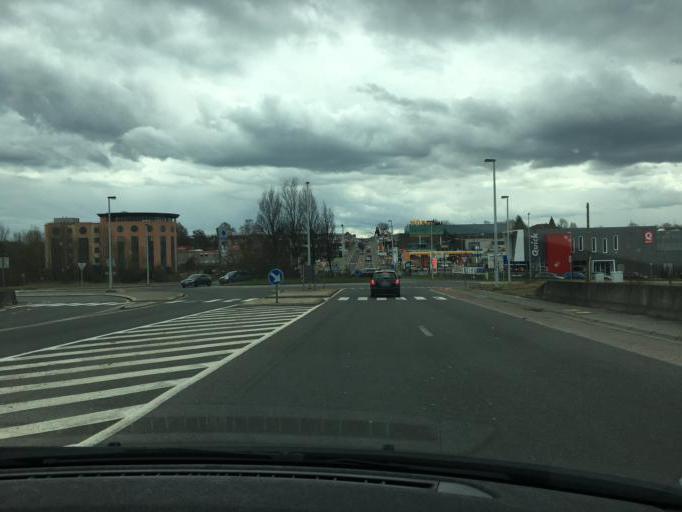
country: BE
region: Wallonia
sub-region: Province de Liege
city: Baelen
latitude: 50.6492
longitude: 6.0012
